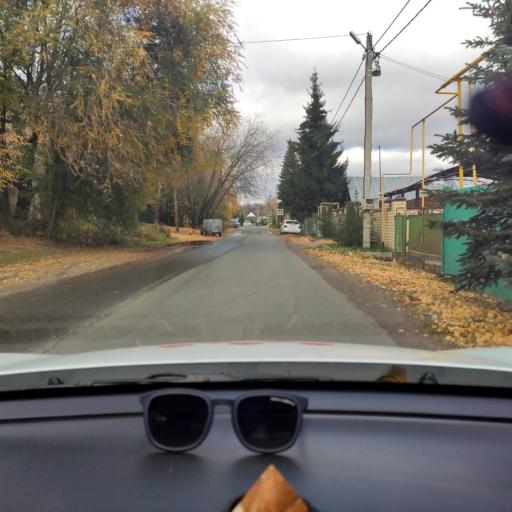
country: RU
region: Tatarstan
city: Verkhniy Uslon
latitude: 55.6203
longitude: 49.0143
